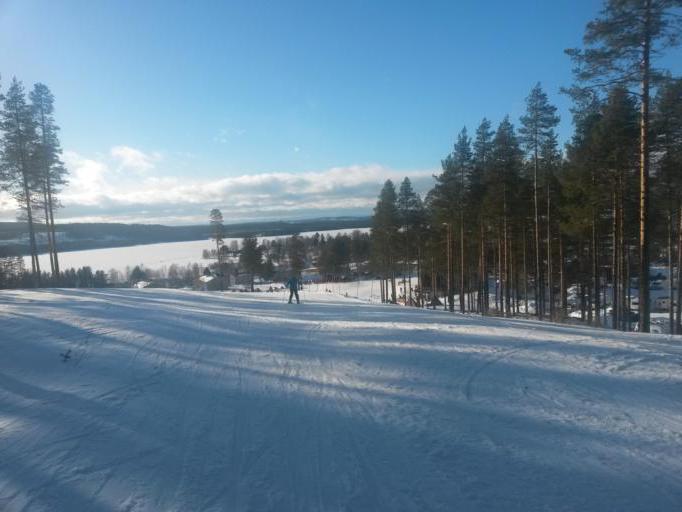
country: SE
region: Vaesterbotten
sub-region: Mala Kommun
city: Mala
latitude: 65.1816
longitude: 18.7546
